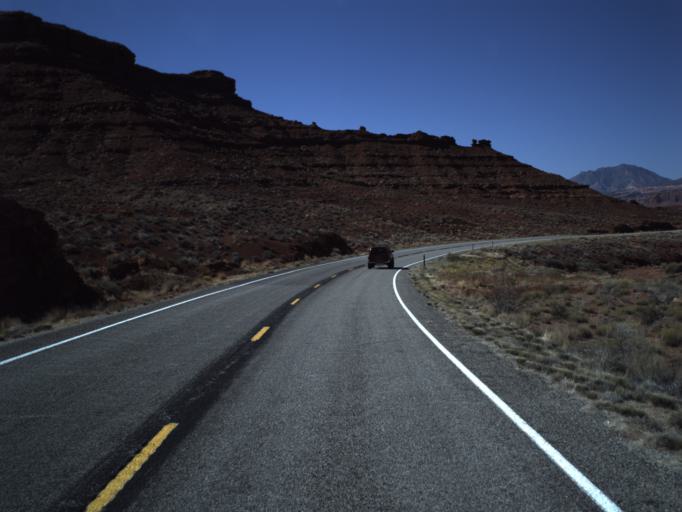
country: US
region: Utah
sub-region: San Juan County
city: Blanding
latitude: 37.8625
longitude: -110.3474
